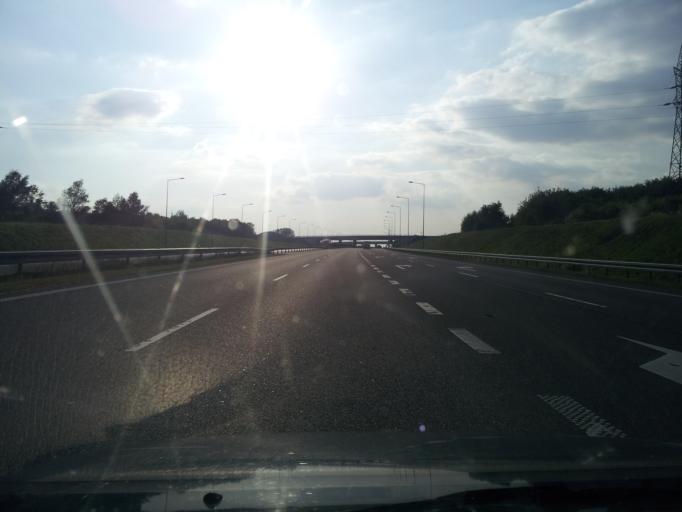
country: PL
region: Lodz Voivodeship
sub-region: Powiat brzezinski
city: Dmosin
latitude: 51.9319
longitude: 19.8002
